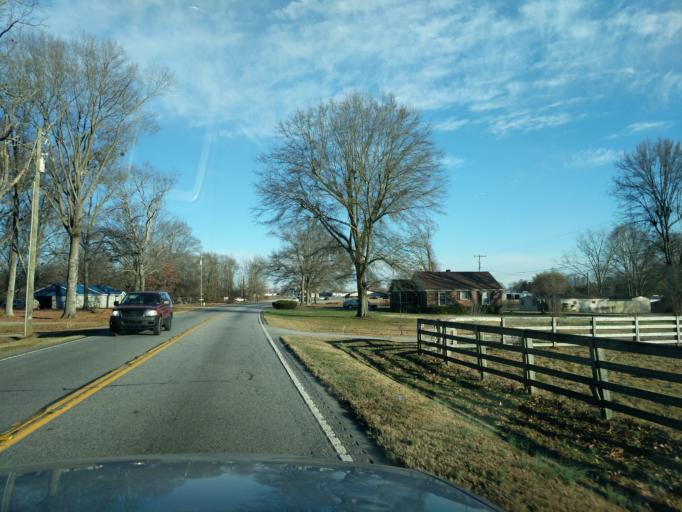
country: US
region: South Carolina
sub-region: Anderson County
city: Williamston
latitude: 34.6681
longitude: -82.5225
